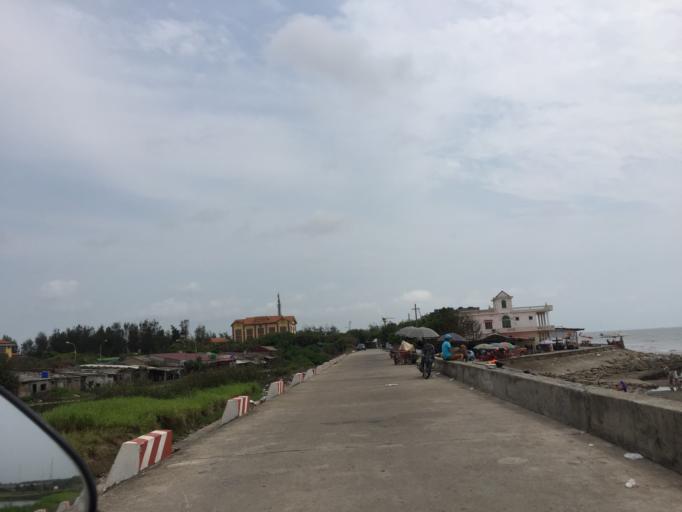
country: VN
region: Ninh Binh
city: Thi Tran Phat Diem
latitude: 20.0219
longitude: 106.2167
